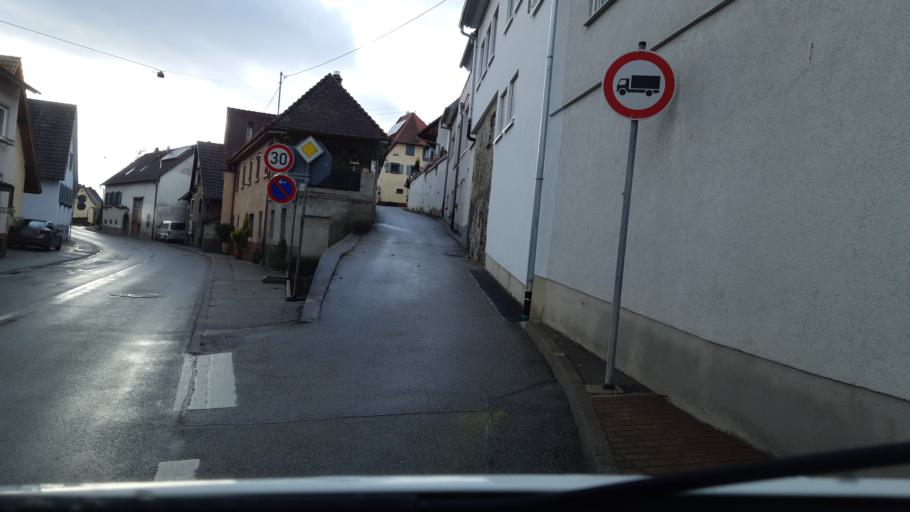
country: DE
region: Baden-Wuerttemberg
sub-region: Freiburg Region
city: Ihringen
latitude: 48.0514
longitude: 7.6809
